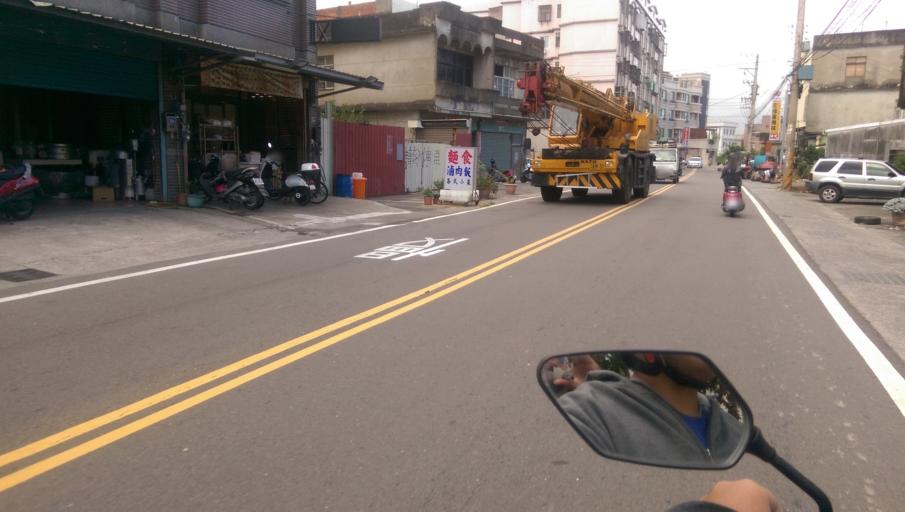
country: TW
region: Taiwan
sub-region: Hsinchu
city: Hsinchu
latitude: 24.8336
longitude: 120.9297
